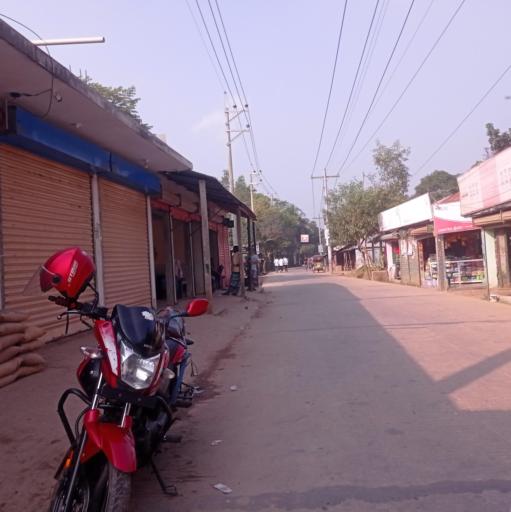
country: BD
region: Dhaka
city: Bhairab Bazar
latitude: 24.0639
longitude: 90.8412
